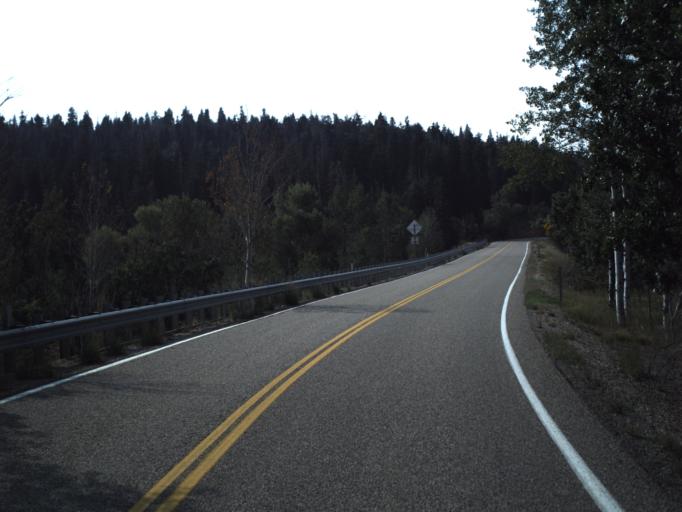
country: US
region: Utah
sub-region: Summit County
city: Summit Park
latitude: 40.8513
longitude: -111.6249
